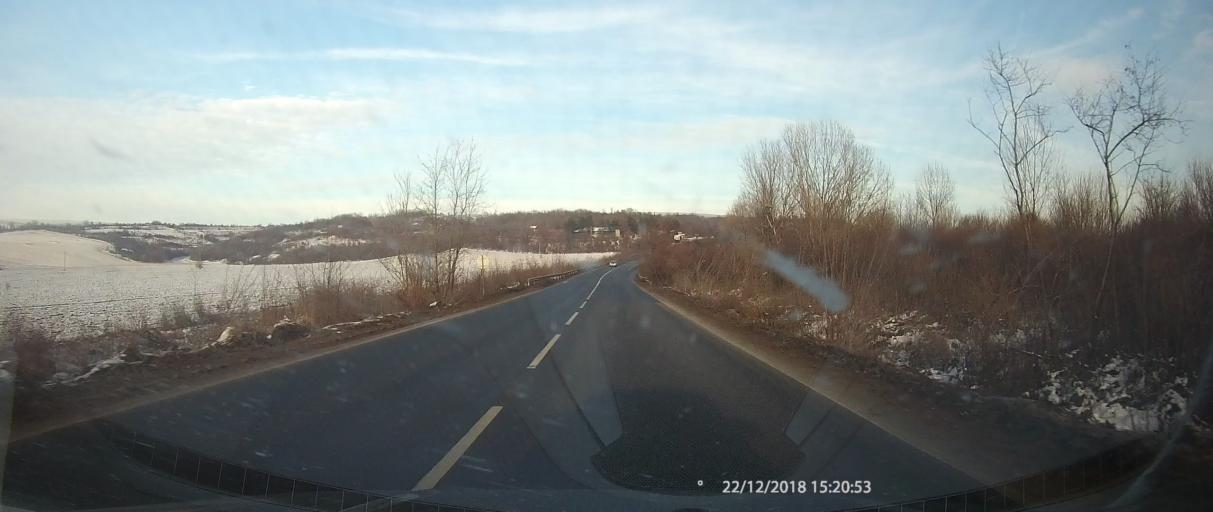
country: BG
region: Ruse
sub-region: Obshtina Dve Mogili
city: Dve Mogili
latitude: 43.6760
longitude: 25.8937
